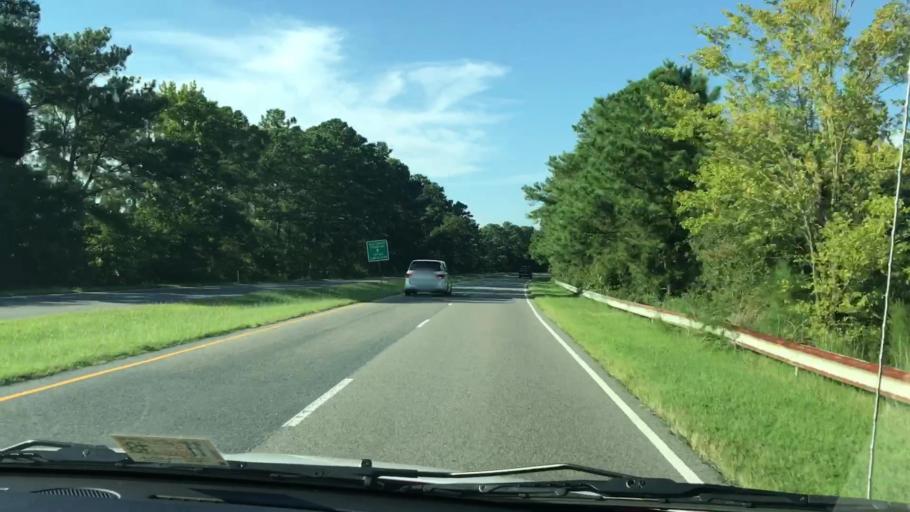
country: US
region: Virginia
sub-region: City of Hampton
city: Hampton
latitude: 37.0547
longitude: -76.3658
